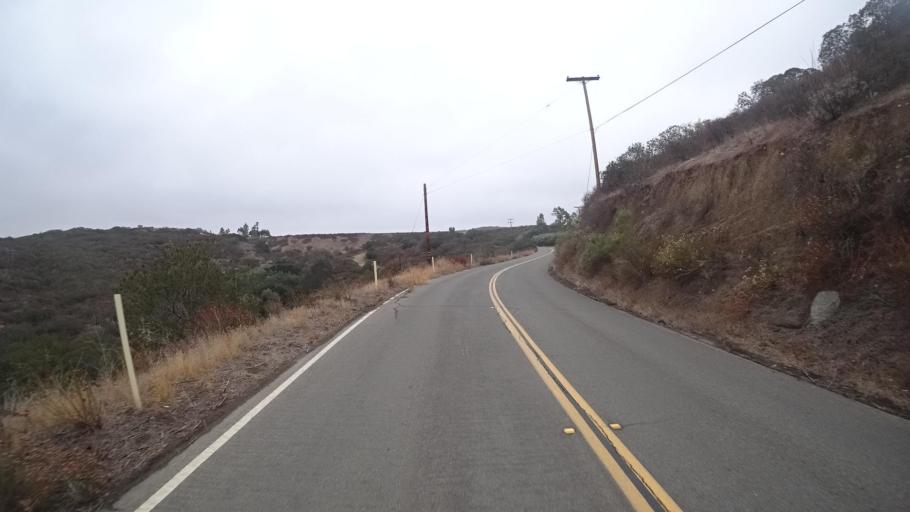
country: US
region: California
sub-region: San Diego County
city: Poway
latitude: 32.9487
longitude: -117.0043
